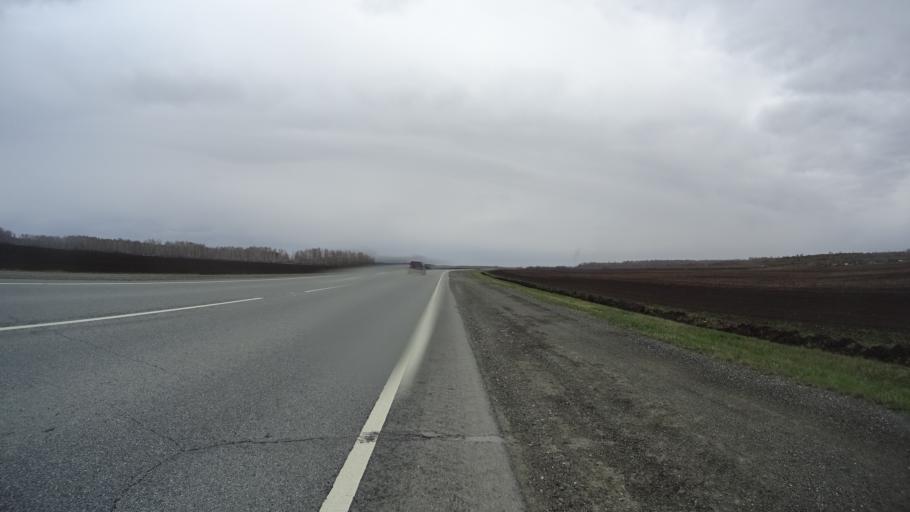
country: RU
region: Chelyabinsk
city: Krasnogorskiy
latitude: 54.5790
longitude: 61.2914
